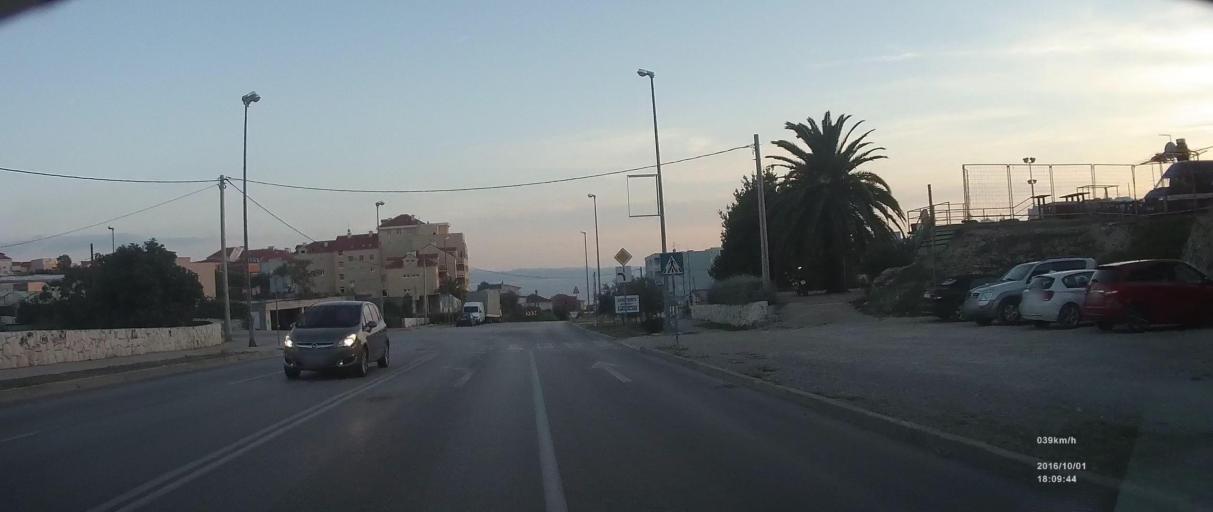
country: HR
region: Splitsko-Dalmatinska
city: Kamen
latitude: 43.5092
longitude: 16.4903
